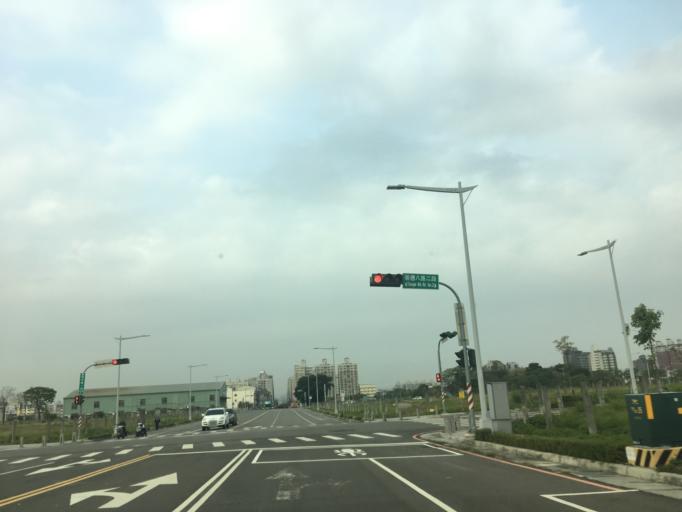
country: TW
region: Taiwan
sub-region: Taichung City
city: Taichung
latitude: 24.1913
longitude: 120.6752
